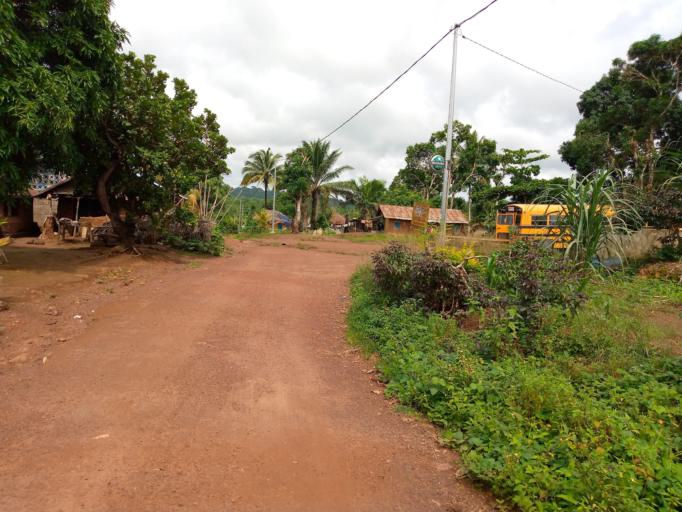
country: SL
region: Southern Province
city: Mogbwemo
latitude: 7.7589
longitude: -12.3084
